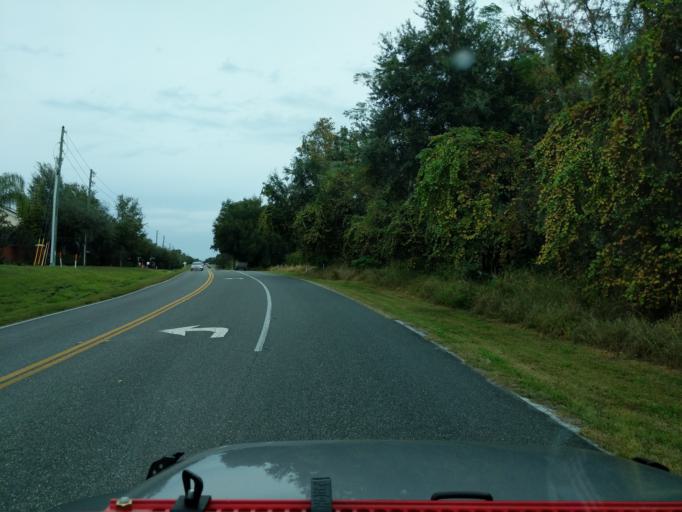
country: US
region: Florida
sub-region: Orange County
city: Oakland
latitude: 28.5315
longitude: -81.6080
